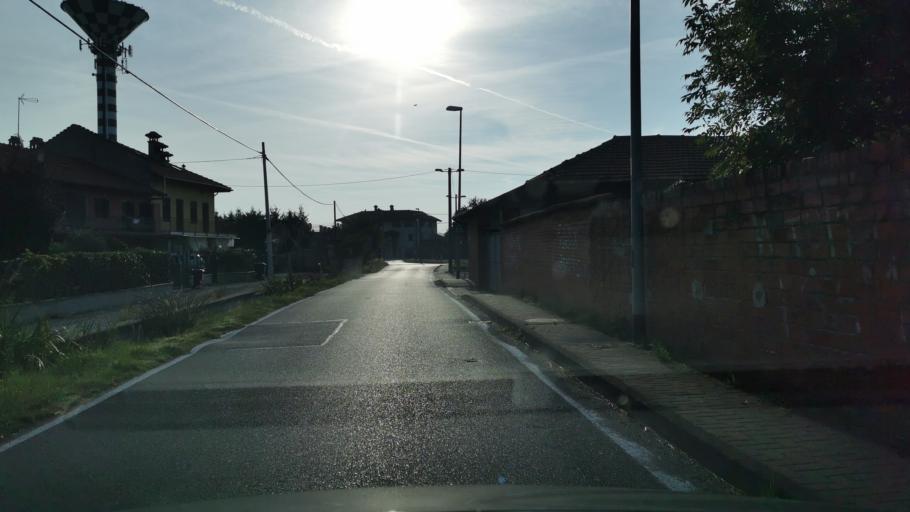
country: IT
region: Piedmont
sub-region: Provincia di Torino
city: Leini
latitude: 45.1559
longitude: 7.6984
